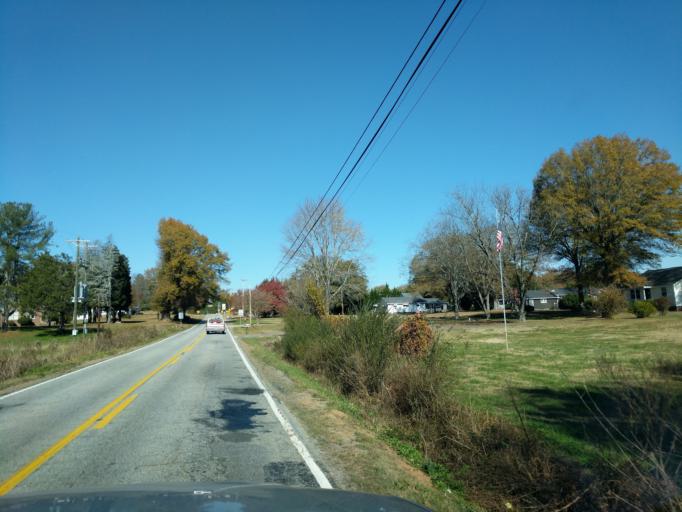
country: US
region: South Carolina
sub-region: Spartanburg County
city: Inman Mills
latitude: 35.0229
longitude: -82.1838
